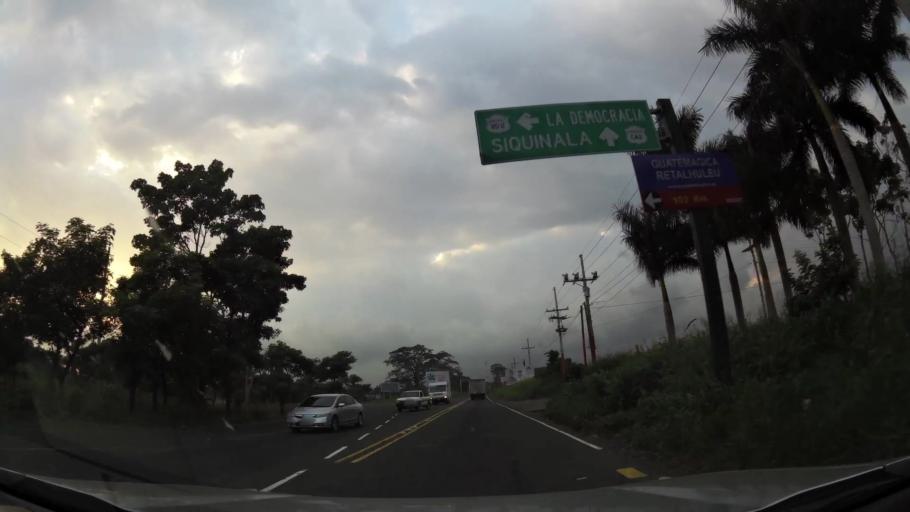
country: GT
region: Escuintla
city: Siquinala
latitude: 14.2976
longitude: -90.9495
